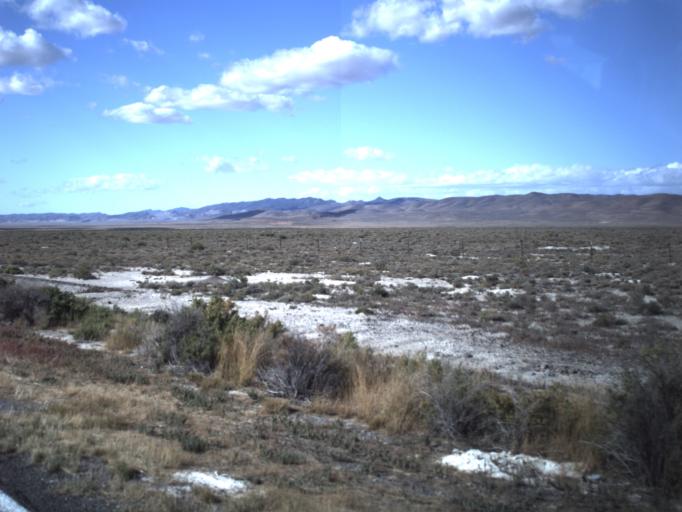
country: US
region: Utah
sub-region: Millard County
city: Delta
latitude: 39.0936
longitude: -112.7502
